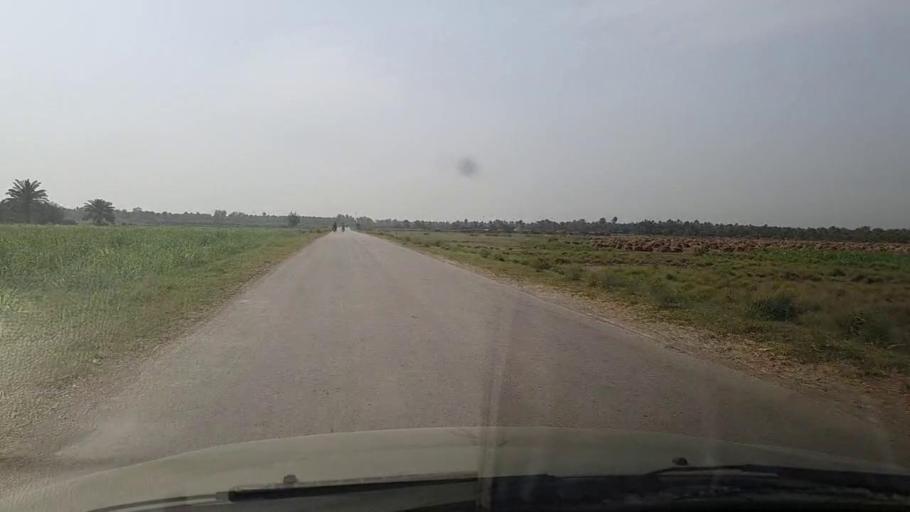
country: PK
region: Sindh
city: Gambat
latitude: 27.4620
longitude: 68.4812
